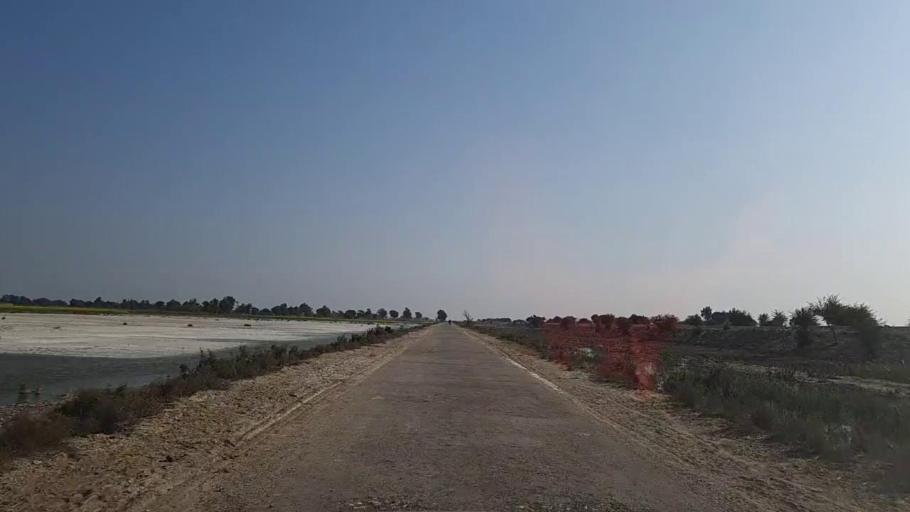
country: PK
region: Sindh
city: Sanghar
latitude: 25.9749
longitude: 69.0281
